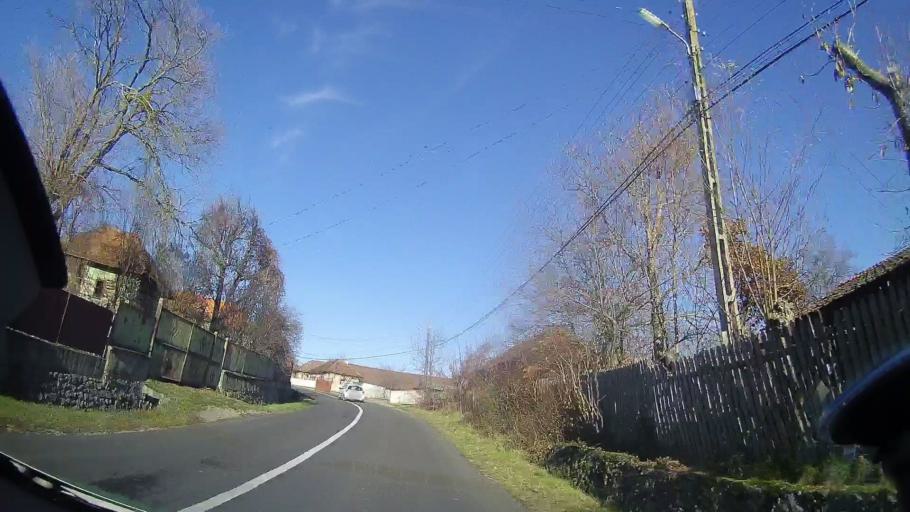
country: RO
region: Bihor
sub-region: Comuna Bratca
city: Beznea
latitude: 46.9633
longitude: 22.6172
